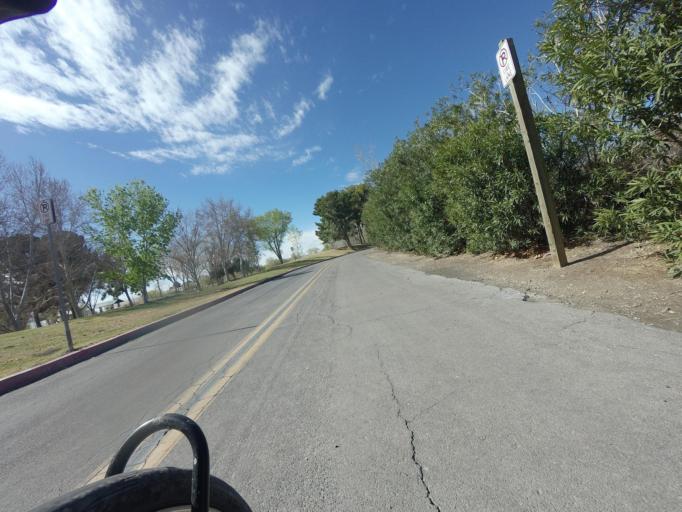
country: US
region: Nevada
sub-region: Clark County
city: North Las Vegas
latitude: 36.3245
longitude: -115.2676
